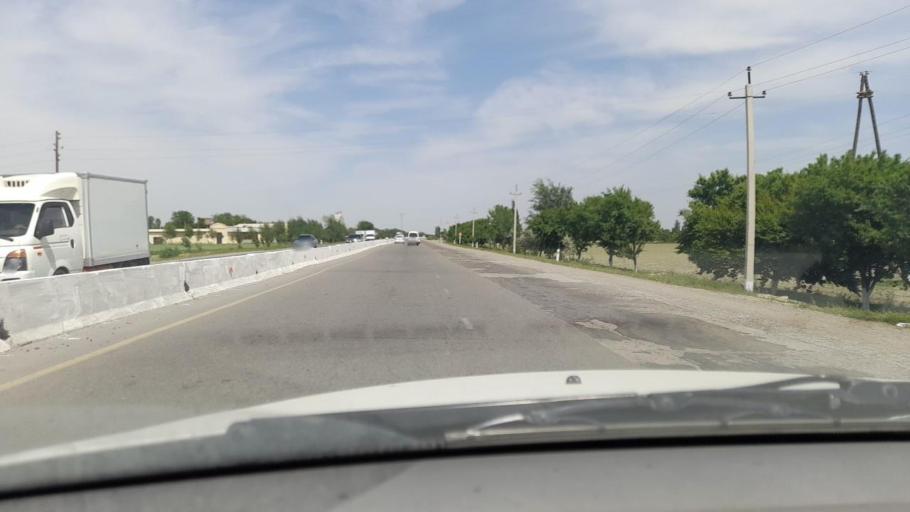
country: UZ
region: Bukhara
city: Wobkent
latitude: 40.0350
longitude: 64.5386
